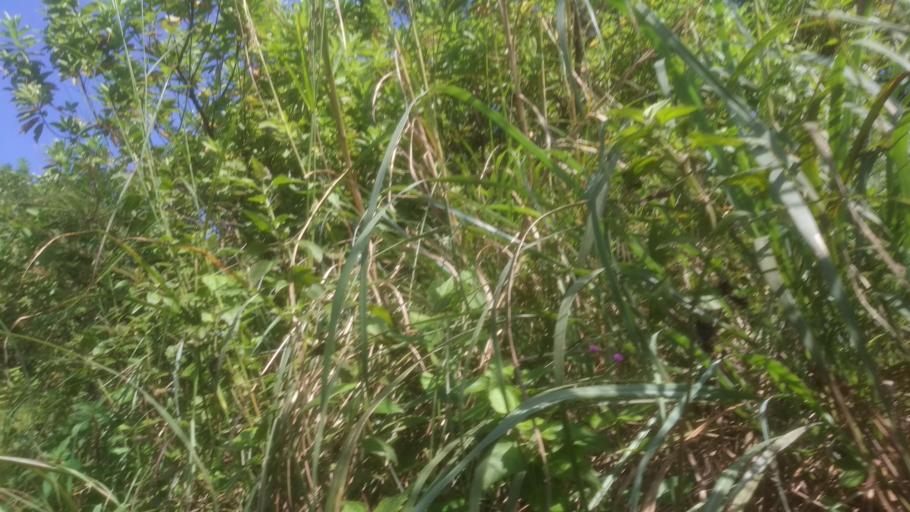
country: IN
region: Kerala
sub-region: Idukki
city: Idukki
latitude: 9.9810
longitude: 76.8307
